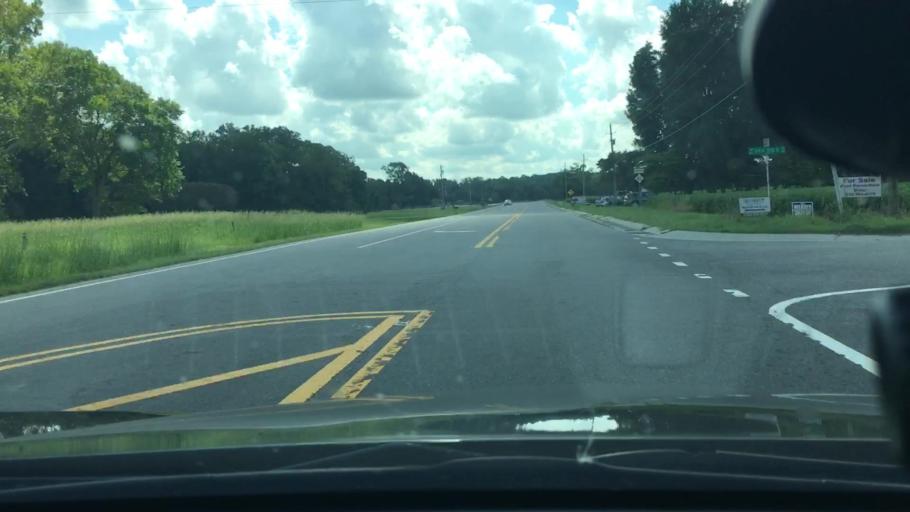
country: US
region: North Carolina
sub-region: Pitt County
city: Summerfield
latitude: 35.6490
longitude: -77.4629
